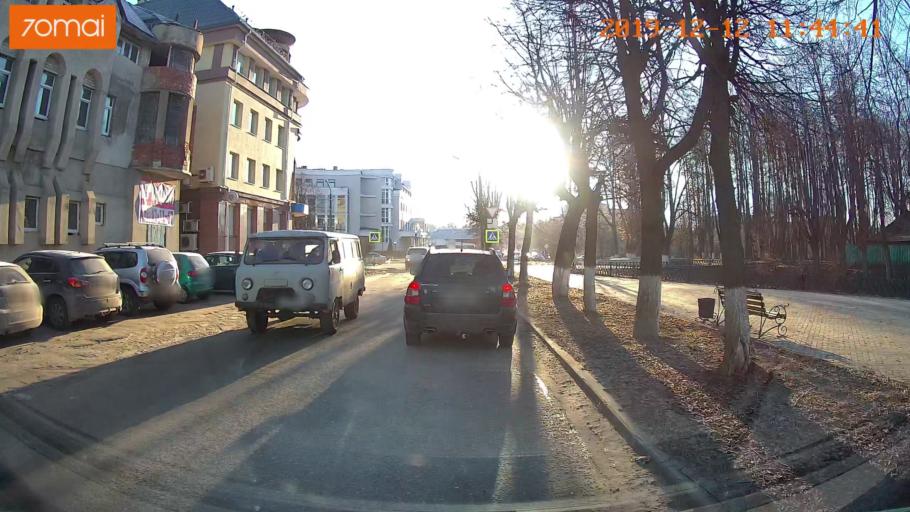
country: RU
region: Ivanovo
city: Shuya
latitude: 56.8538
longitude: 41.3748
